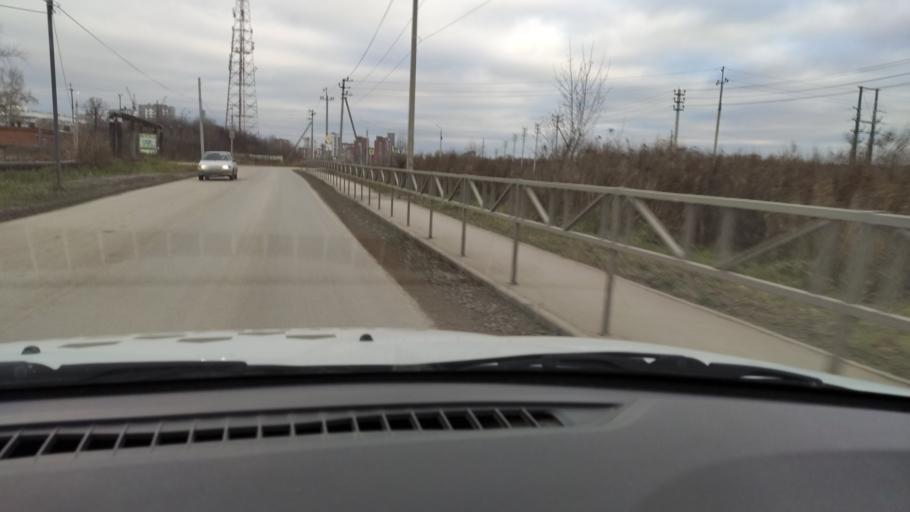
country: RU
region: Perm
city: Kondratovo
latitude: 57.9831
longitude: 56.1152
